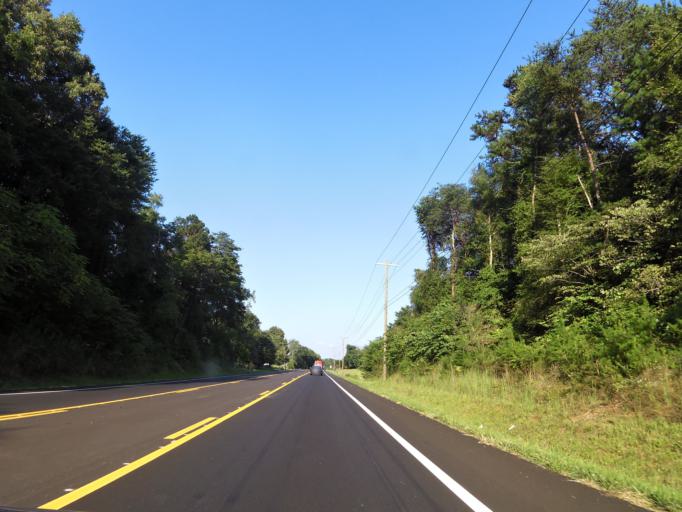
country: US
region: Tennessee
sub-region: Knox County
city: Knoxville
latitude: 35.8891
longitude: -83.9170
